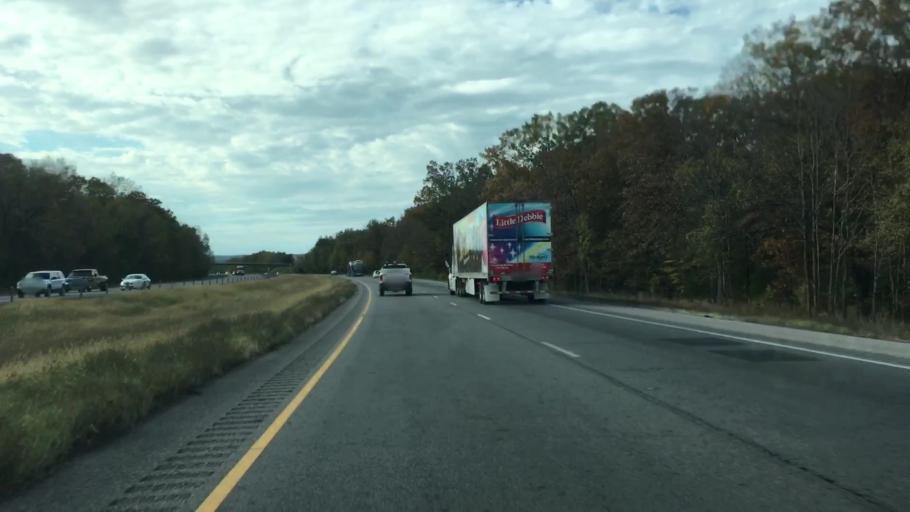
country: US
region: Arkansas
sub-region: Pope County
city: Atkins
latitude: 35.2460
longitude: -92.8665
